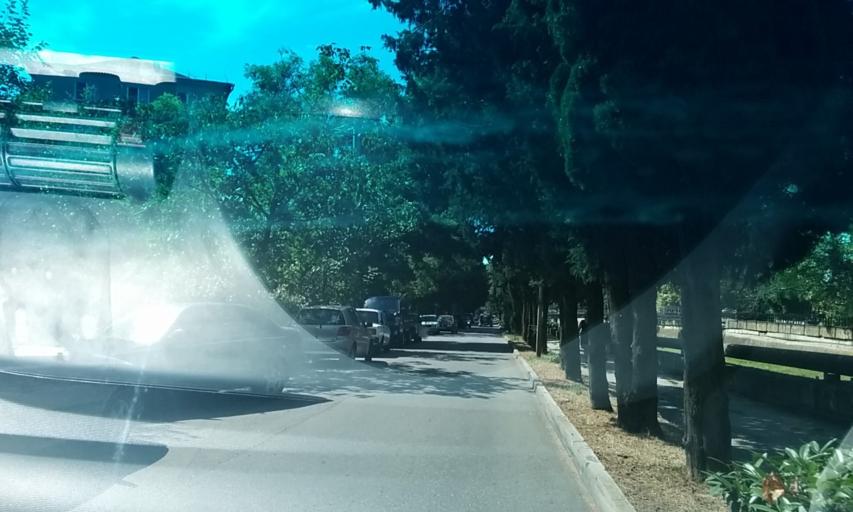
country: RU
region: Krasnodarskiy
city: Tuapse
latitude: 44.1089
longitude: 39.0612
